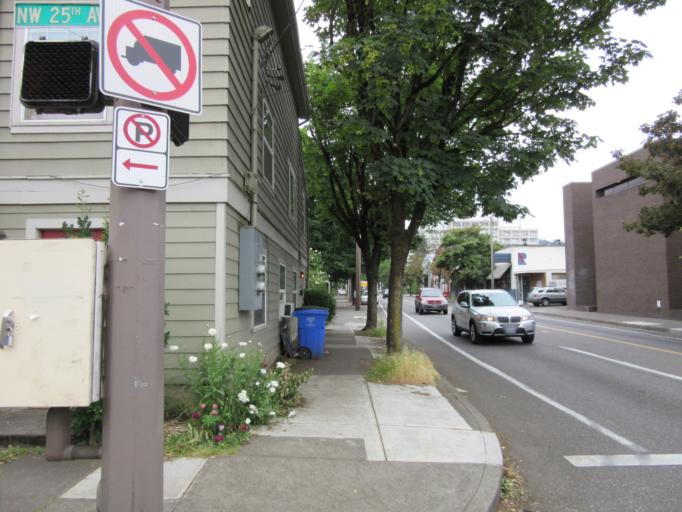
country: US
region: Oregon
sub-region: Multnomah County
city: Portland
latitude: 45.5368
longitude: -122.7029
